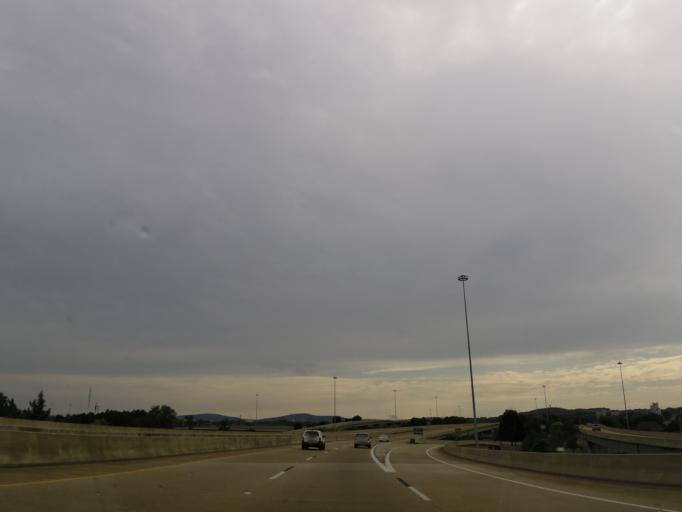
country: US
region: Alabama
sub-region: Madison County
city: Huntsville
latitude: 34.7395
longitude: -86.5863
